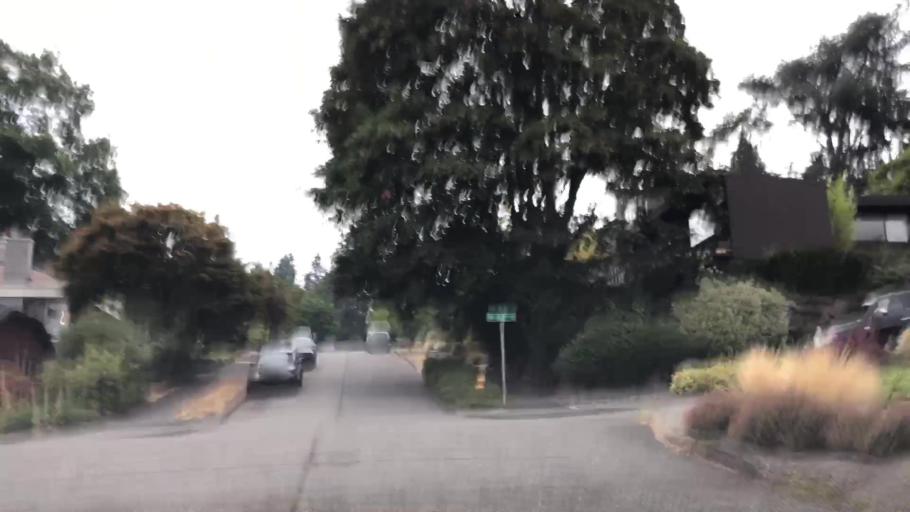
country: US
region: Washington
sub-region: King County
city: Yarrow Point
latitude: 47.6599
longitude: -122.2730
